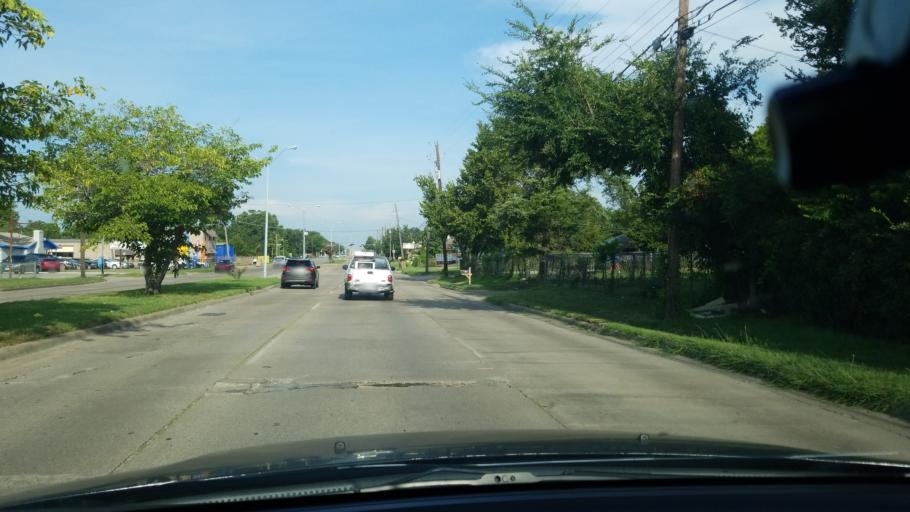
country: US
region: Texas
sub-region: Dallas County
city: Balch Springs
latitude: 32.7342
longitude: -96.6353
